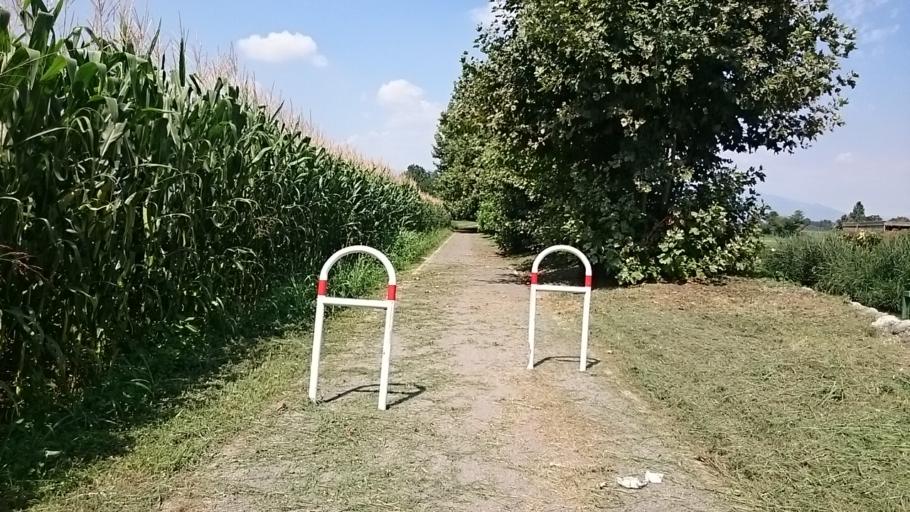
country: IT
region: Veneto
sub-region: Provincia di Vicenza
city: Rosa
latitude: 45.7117
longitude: 11.7371
